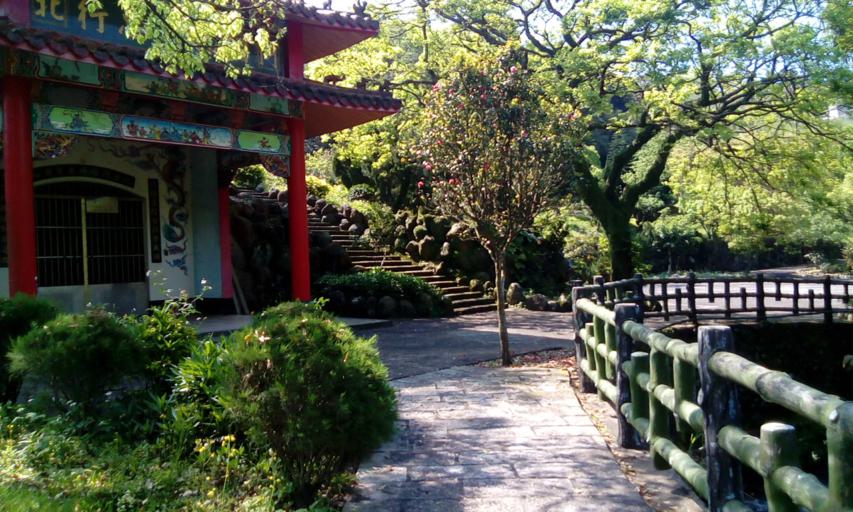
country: TW
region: Taipei
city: Taipei
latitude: 25.2027
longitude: 121.4827
